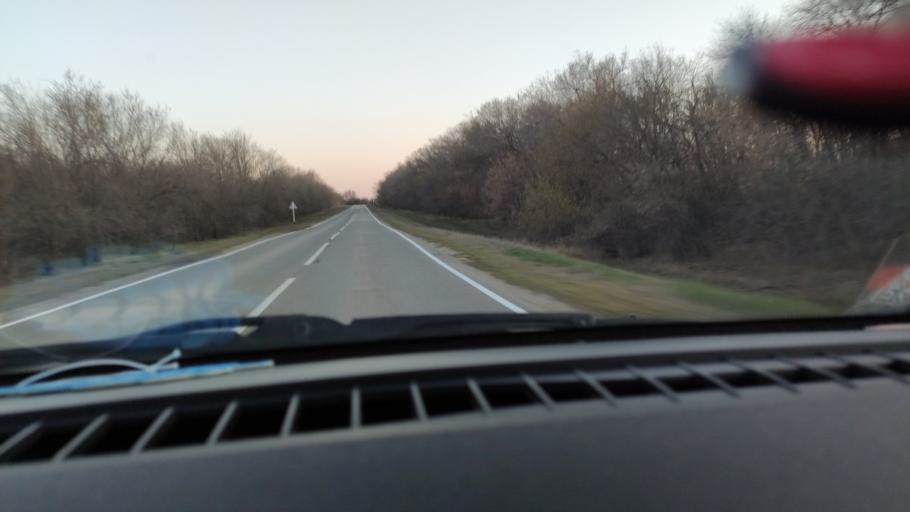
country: RU
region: Saratov
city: Privolzhskiy
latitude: 51.2243
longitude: 45.9203
